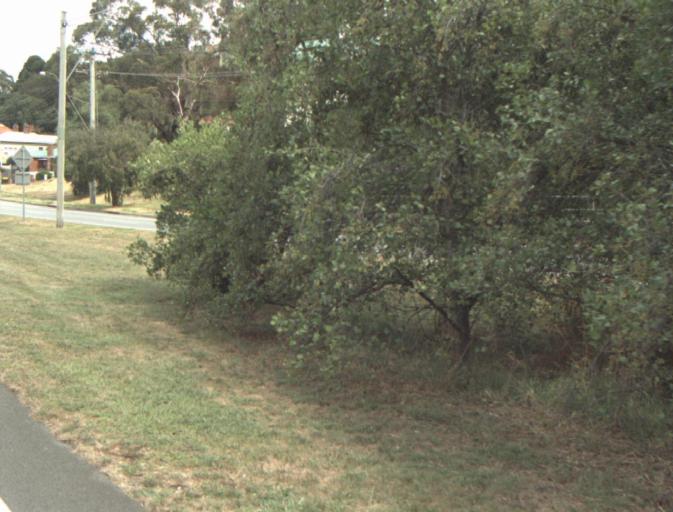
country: AU
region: Tasmania
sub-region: Launceston
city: Launceston
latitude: -41.4324
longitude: 147.1217
